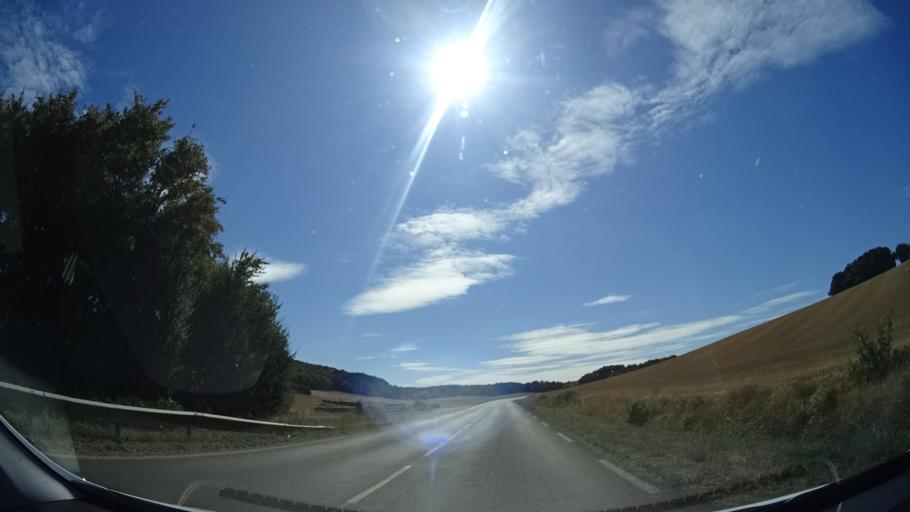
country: FR
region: Bourgogne
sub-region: Departement de l'Yonne
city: Saint-Julien-du-Sault
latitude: 47.9324
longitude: 3.2276
